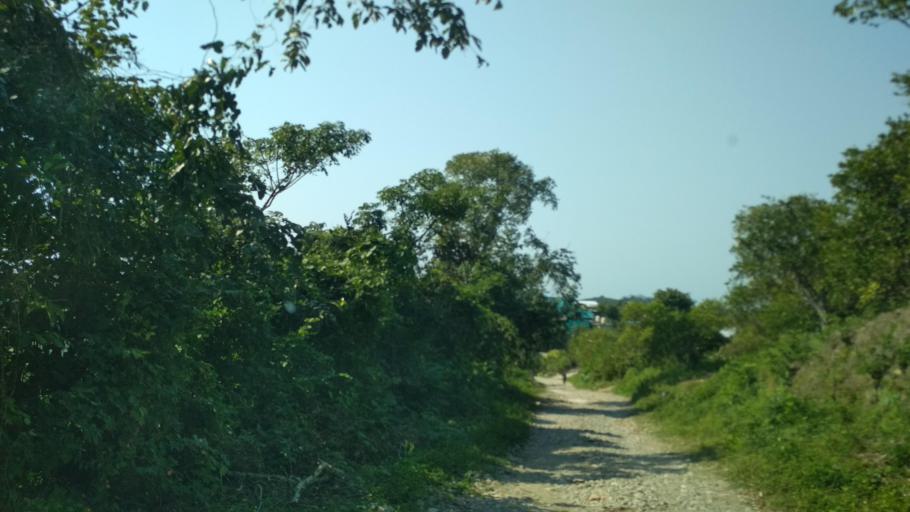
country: MX
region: Veracruz
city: Agua Dulce
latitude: 20.3868
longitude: -97.2128
